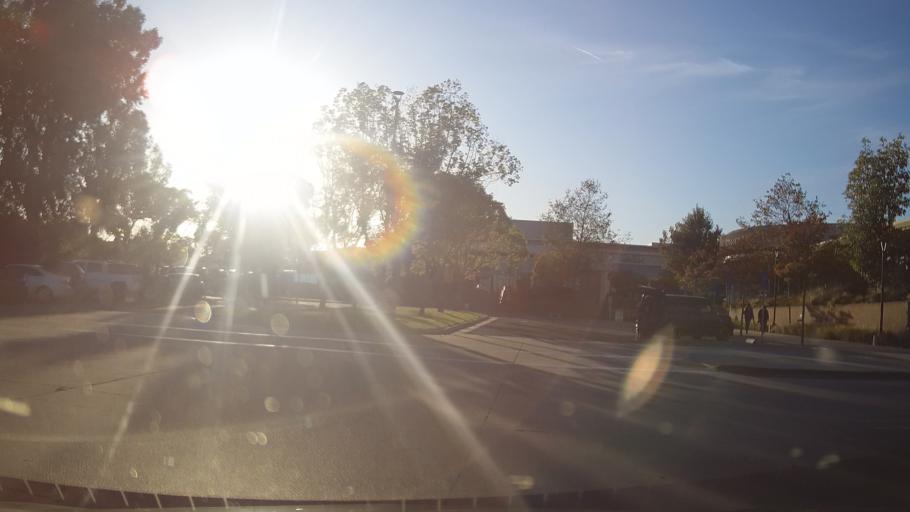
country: US
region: California
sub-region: San Diego County
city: Santee
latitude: 32.8148
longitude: -117.0055
